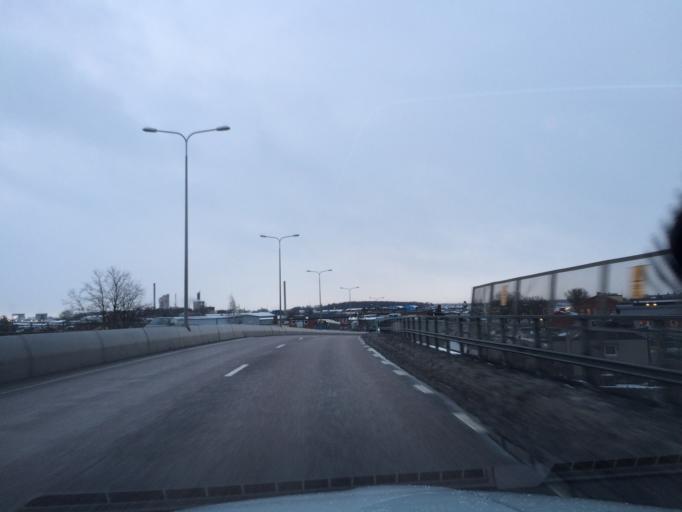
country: SE
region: Vaestmanland
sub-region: Kopings Kommun
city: Koping
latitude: 59.5082
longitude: 15.9932
